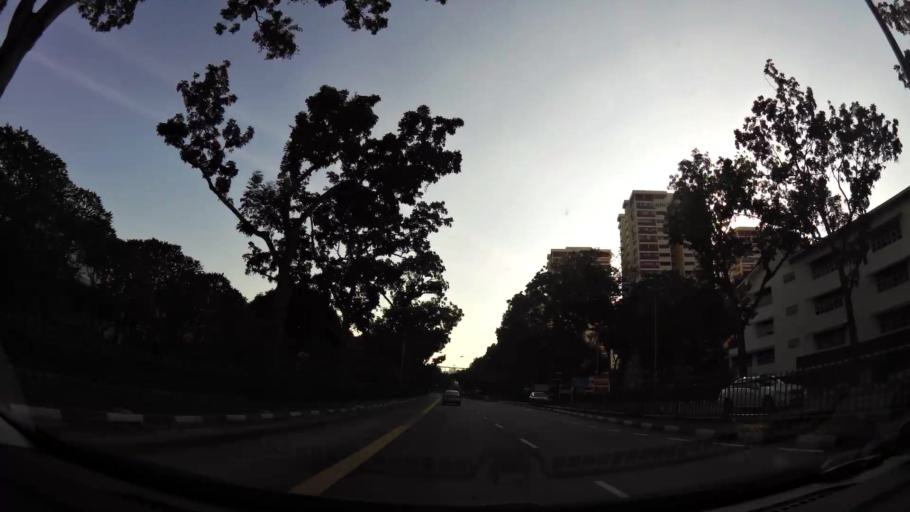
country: SG
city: Singapore
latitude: 1.3079
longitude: 103.9201
